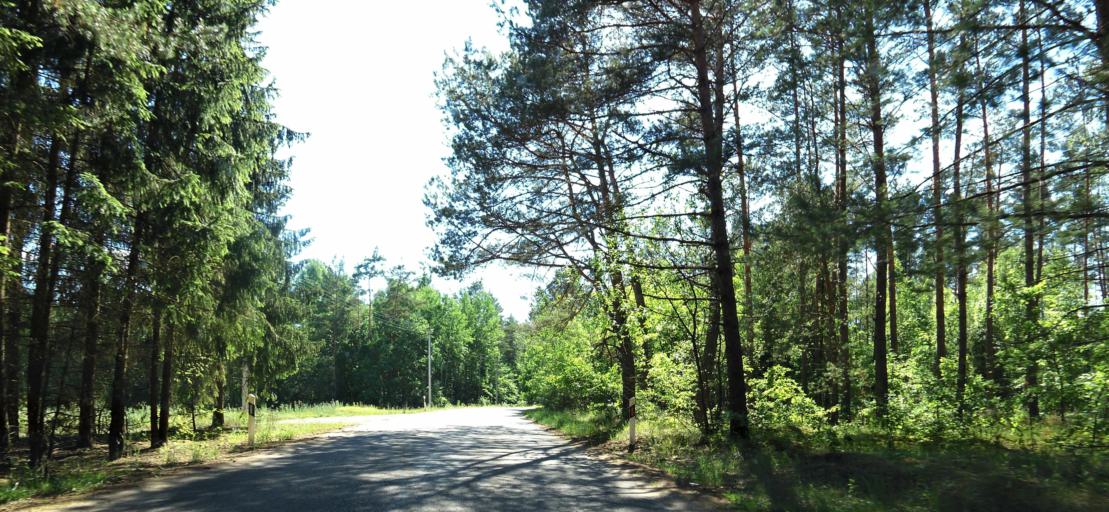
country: LT
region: Vilnius County
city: Rasos
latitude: 54.7528
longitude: 25.3312
